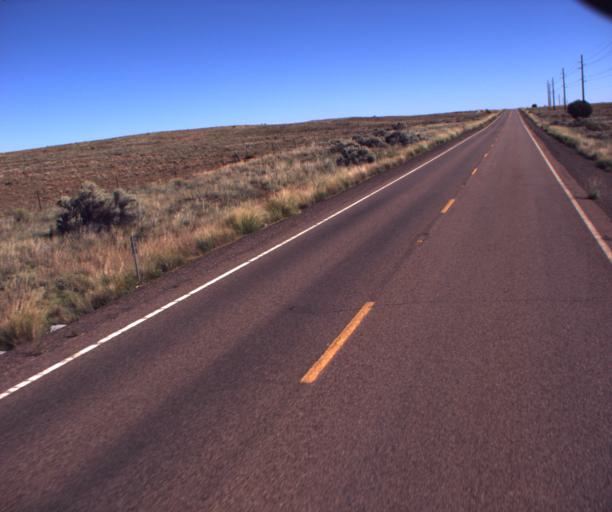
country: US
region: Arizona
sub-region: Navajo County
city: Taylor
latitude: 34.4881
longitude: -110.2365
